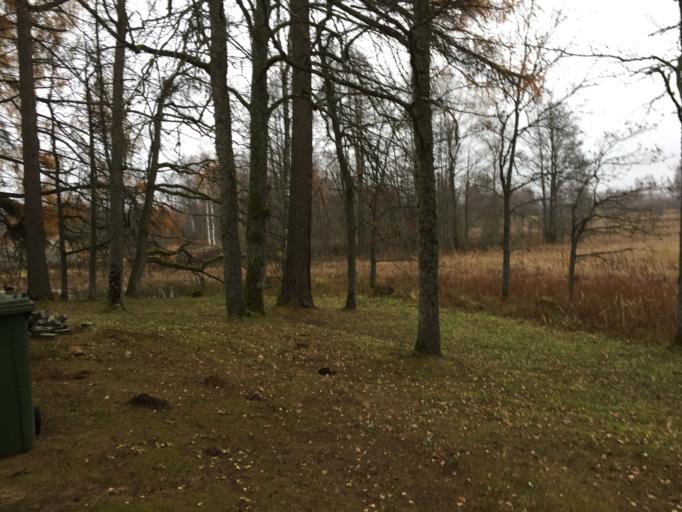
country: LV
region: Pargaujas
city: Stalbe
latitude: 57.5070
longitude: 25.0027
